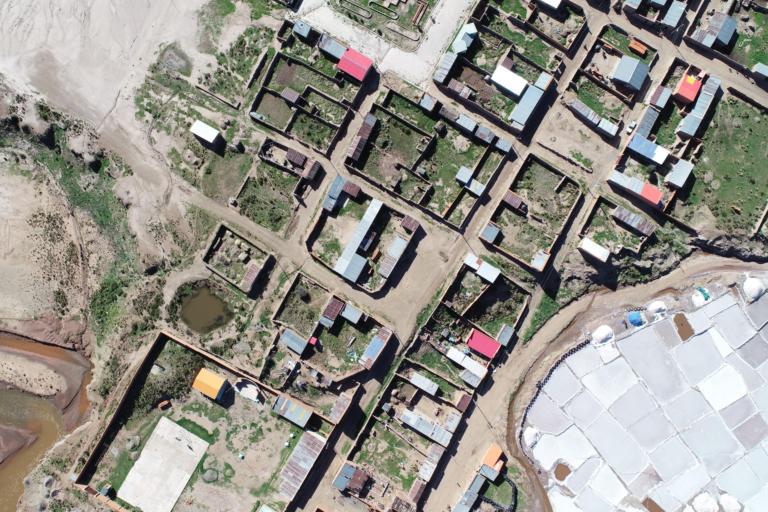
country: BO
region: La Paz
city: Patacamaya
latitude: -17.2989
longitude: -68.4826
